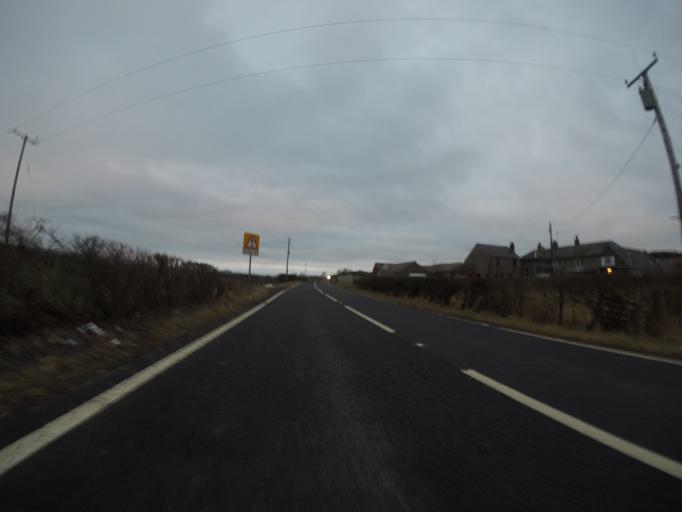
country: GB
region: Scotland
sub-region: North Ayrshire
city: Dalry
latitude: 55.6921
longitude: -4.7432
